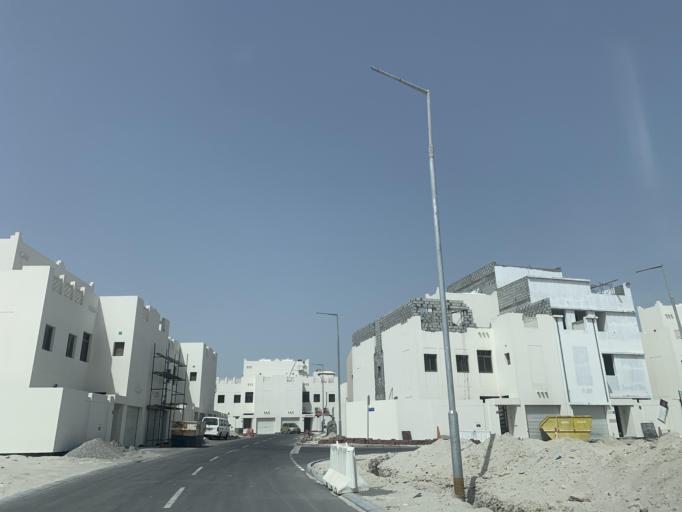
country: BH
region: Northern
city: Ar Rifa'
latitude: 26.1484
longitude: 50.5648
